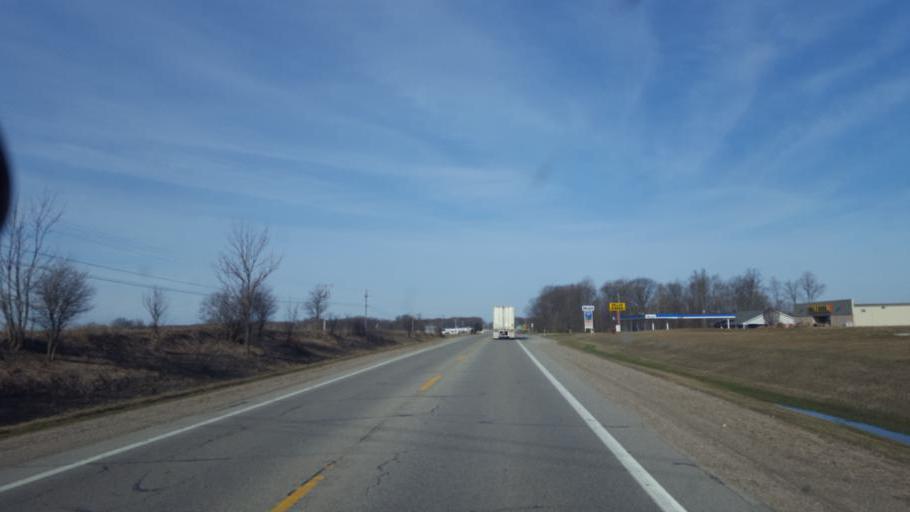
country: US
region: Michigan
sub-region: Montcalm County
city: Lakeview
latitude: 43.4314
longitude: -85.2555
